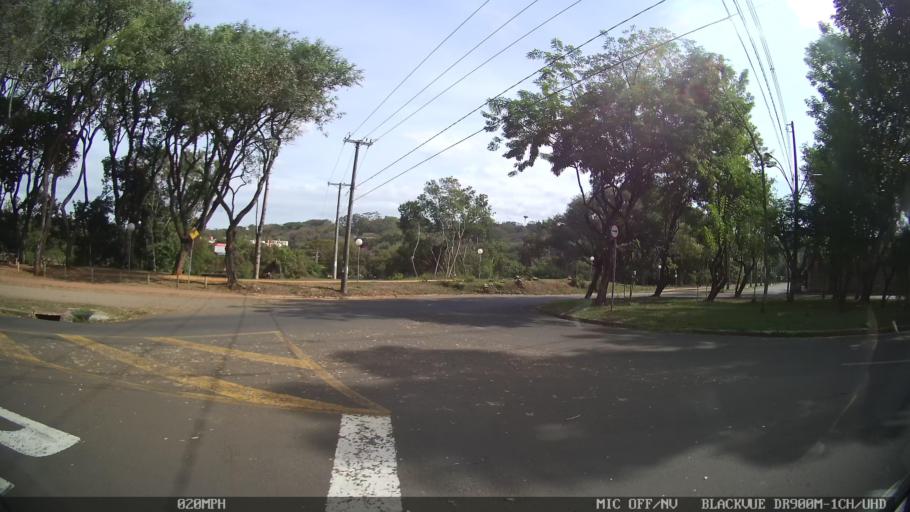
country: BR
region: Sao Paulo
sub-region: Piracicaba
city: Piracicaba
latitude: -22.7190
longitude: -47.6742
